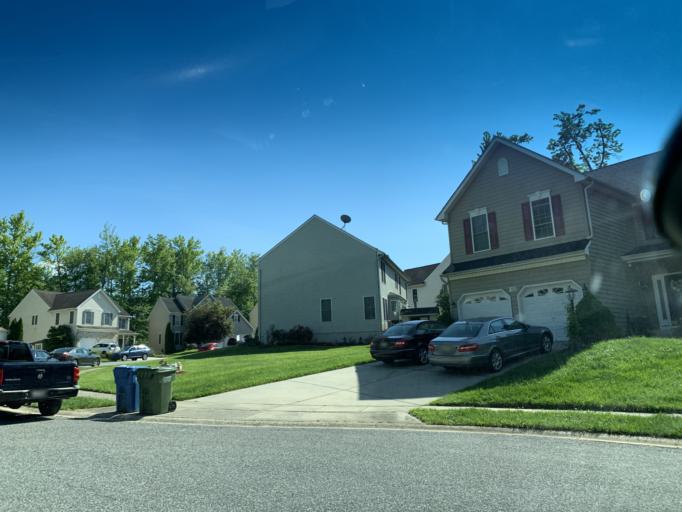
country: US
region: Maryland
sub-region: Harford County
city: Riverside
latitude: 39.4903
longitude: -76.2210
